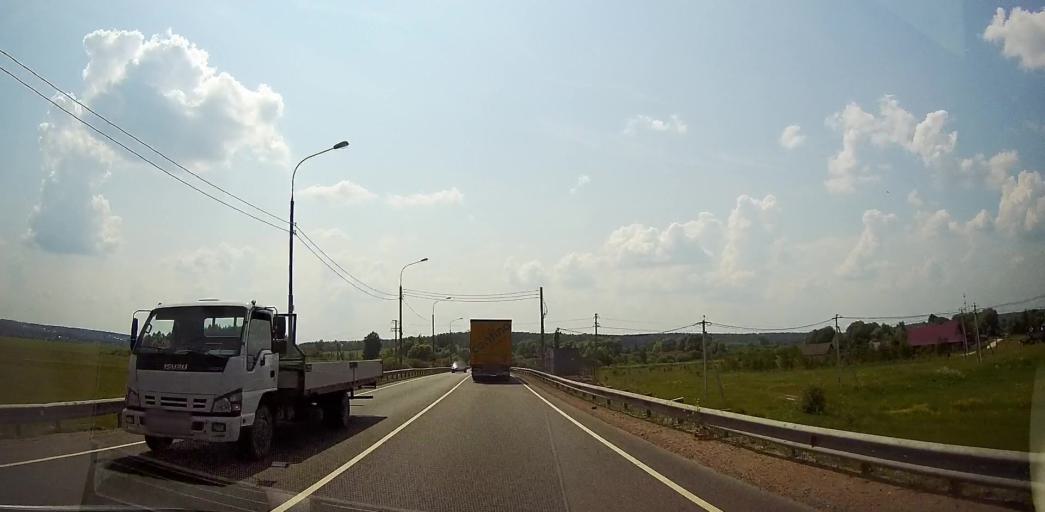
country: RU
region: Moskovskaya
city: Meshcherino
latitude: 55.1894
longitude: 38.3600
